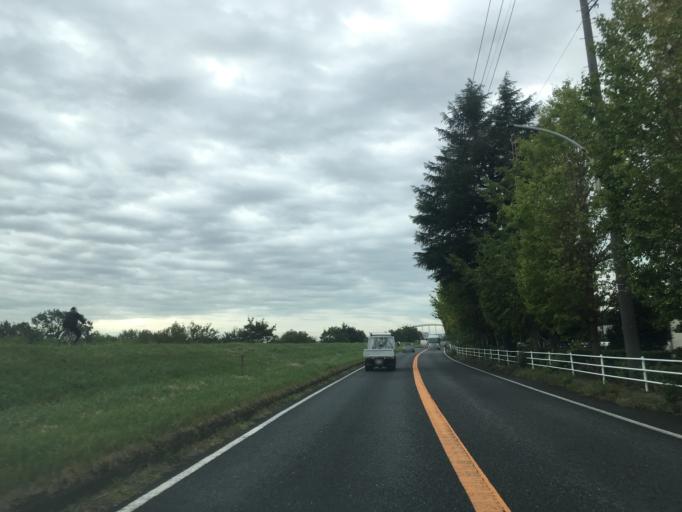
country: JP
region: Tokyo
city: Chofugaoka
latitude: 35.6312
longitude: 139.5621
